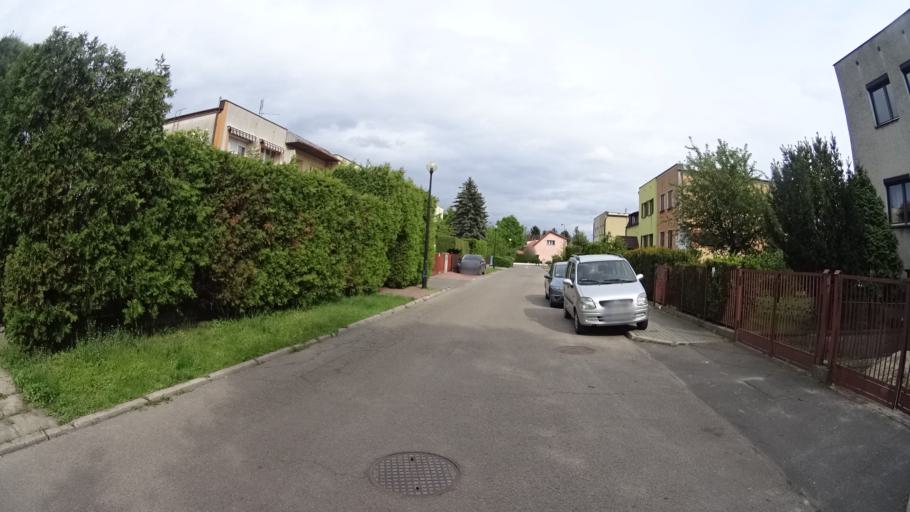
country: PL
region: Masovian Voivodeship
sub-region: Powiat warszawski zachodni
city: Babice
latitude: 52.2496
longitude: 20.8747
